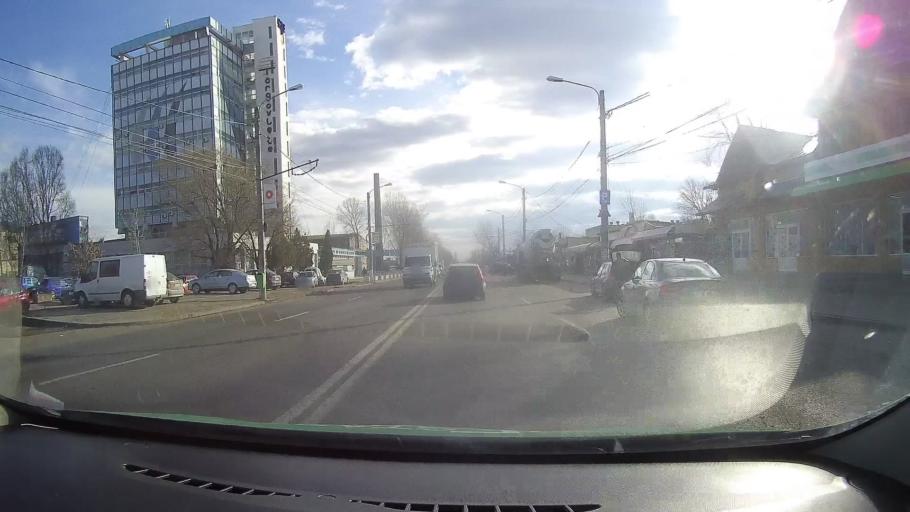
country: RO
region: Dambovita
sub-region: Comuna Lucieni
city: Lucieni
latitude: 44.8505
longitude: 25.4360
